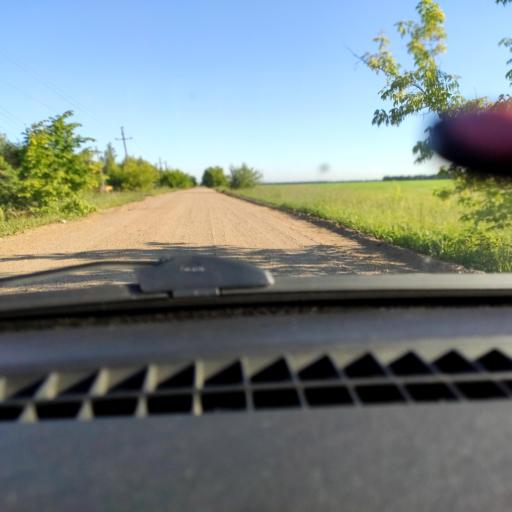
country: RU
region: Bashkortostan
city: Iglino
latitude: 54.7533
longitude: 56.3367
